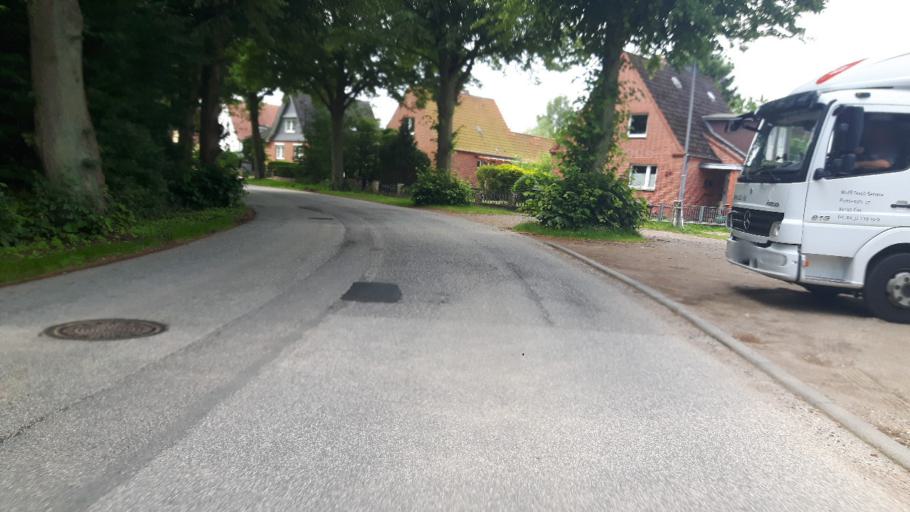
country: DE
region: Schleswig-Holstein
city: Travemuende
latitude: 53.9412
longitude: 10.8440
